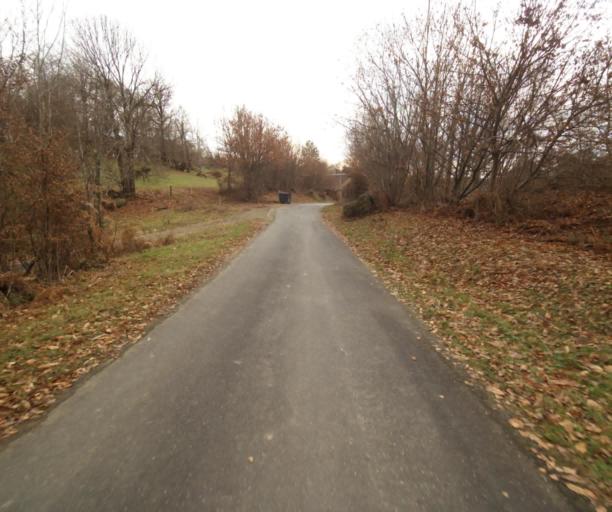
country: FR
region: Limousin
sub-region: Departement de la Correze
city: Chameyrat
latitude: 45.2601
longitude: 1.7060
